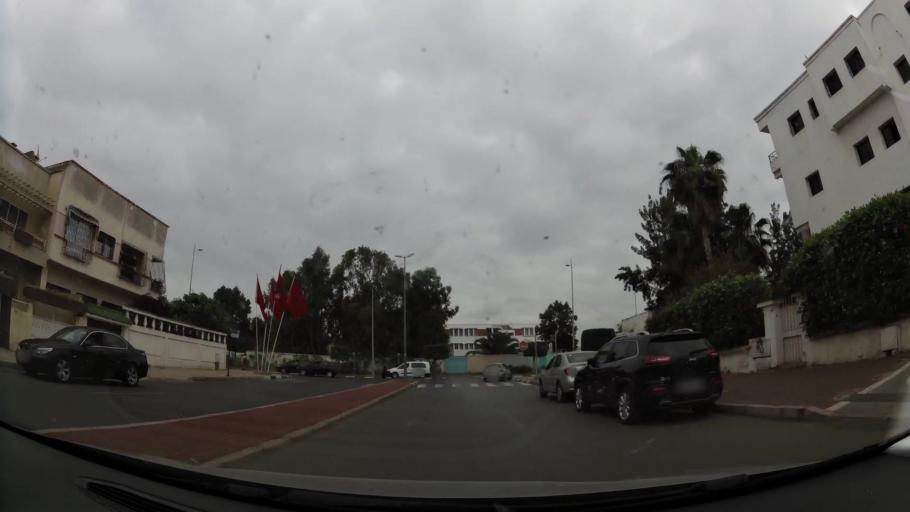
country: MA
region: Rabat-Sale-Zemmour-Zaer
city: Sale
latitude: 34.0289
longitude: -6.8005
